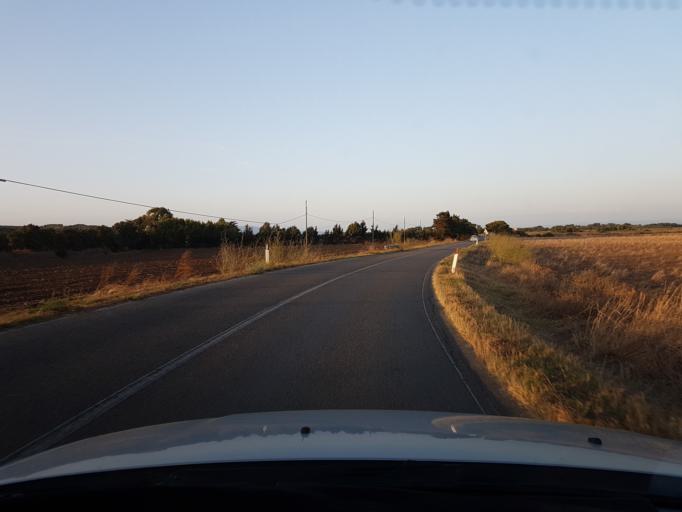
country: IT
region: Sardinia
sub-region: Provincia di Oristano
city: Cabras
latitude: 39.9104
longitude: 8.4395
